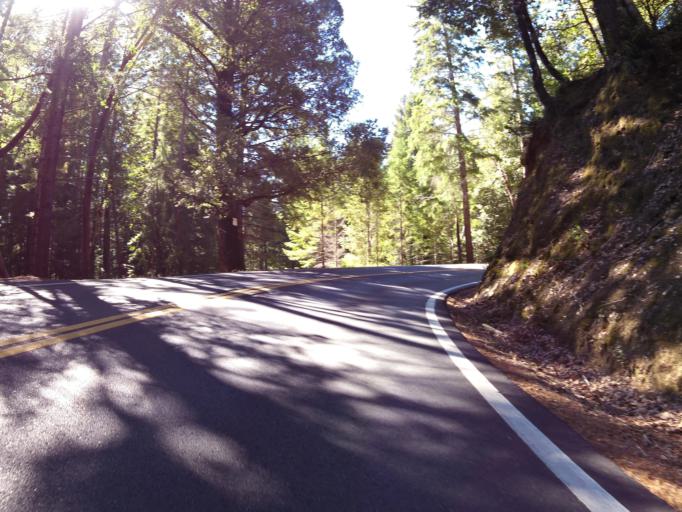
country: US
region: California
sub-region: Humboldt County
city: Redway
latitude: 39.8504
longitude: -123.7297
